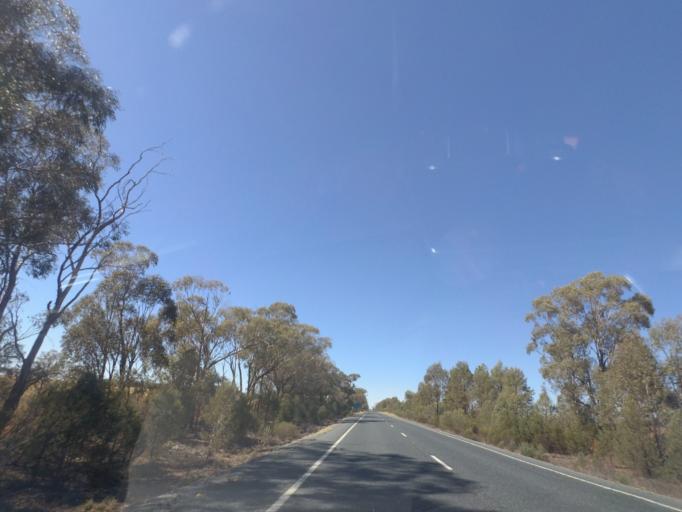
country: AU
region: New South Wales
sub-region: Bland
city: West Wyalong
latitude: -34.1554
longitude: 147.1177
